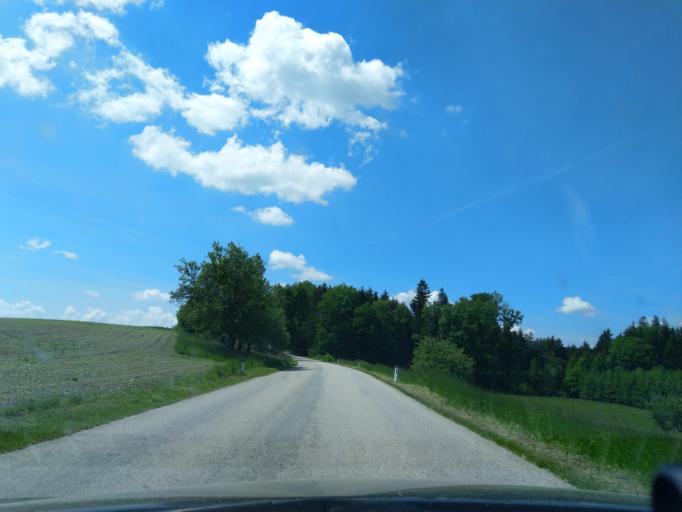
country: AT
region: Upper Austria
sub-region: Politischer Bezirk Ried im Innkreis
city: Ried im Innkreis
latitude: 48.1998
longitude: 13.5905
